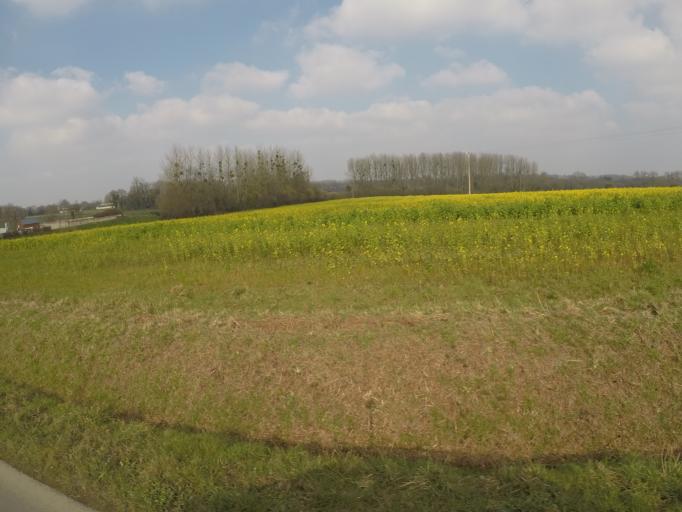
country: FR
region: Brittany
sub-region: Departement des Cotes-d'Armor
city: Pommerit-le-Vicomte
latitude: 48.6170
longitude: -3.0711
